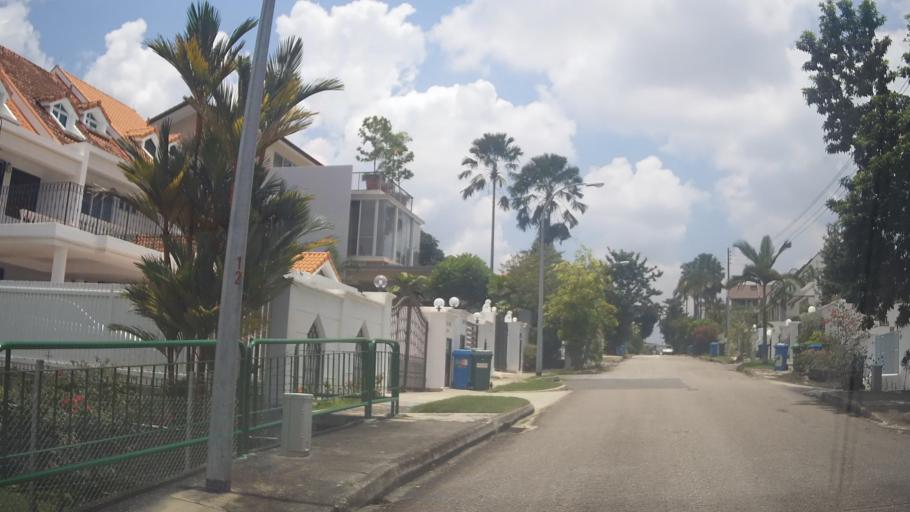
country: SG
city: Singapore
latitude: 1.3610
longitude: 103.8705
